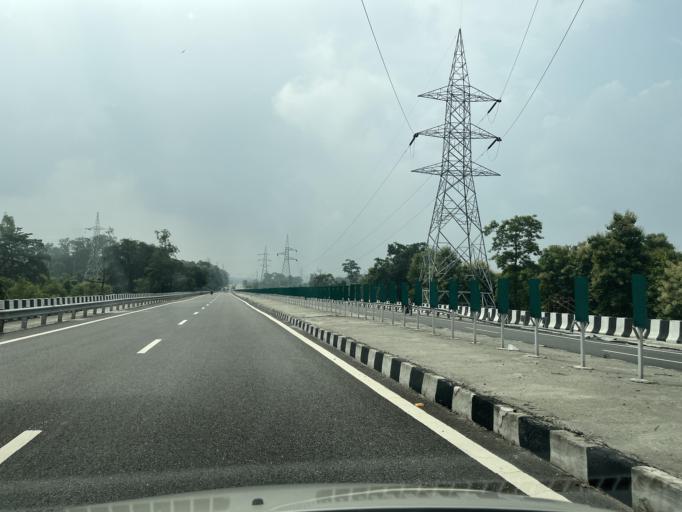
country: IN
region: Uttarakhand
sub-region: Dehradun
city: Raiwala
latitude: 30.0968
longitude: 78.1806
